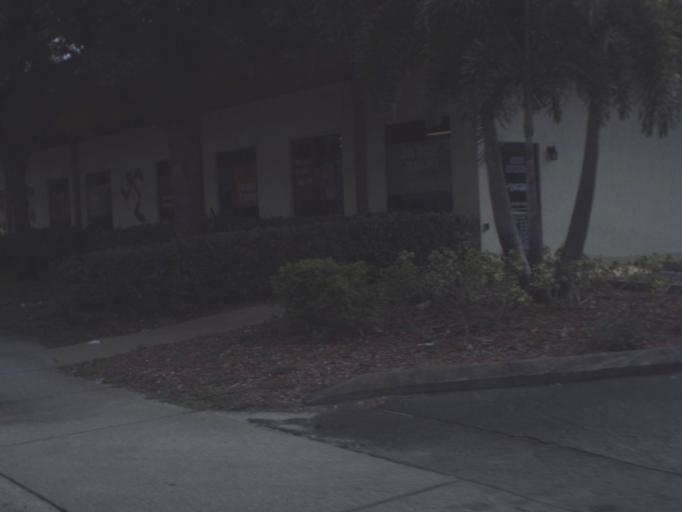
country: US
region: Florida
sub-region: Pinellas County
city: Gandy
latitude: 27.8343
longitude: -82.6386
